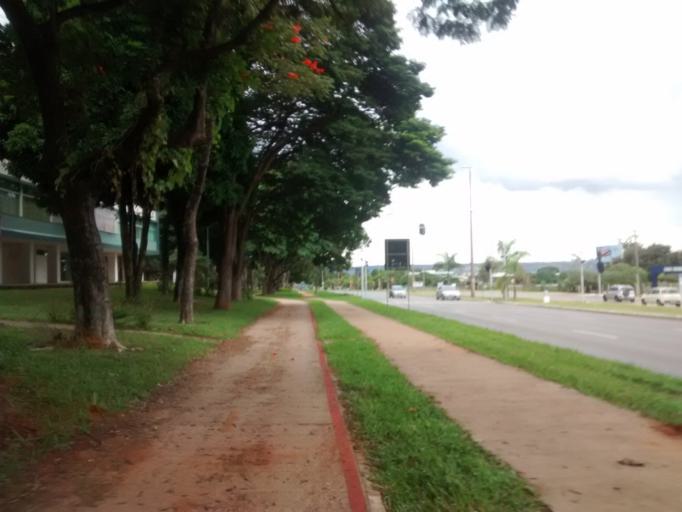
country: BR
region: Federal District
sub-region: Brasilia
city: Brasilia
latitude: -15.7698
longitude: -47.8754
